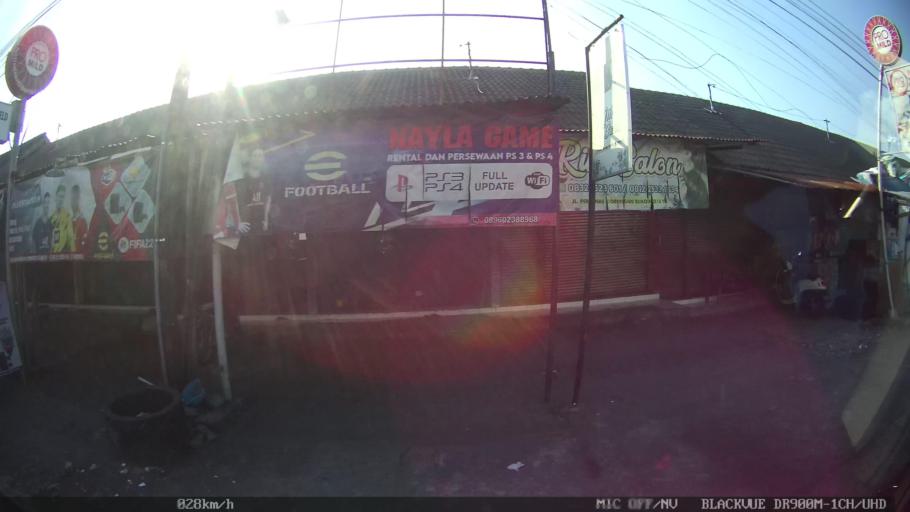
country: ID
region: Daerah Istimewa Yogyakarta
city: Depok
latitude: -7.7626
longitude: 110.4066
